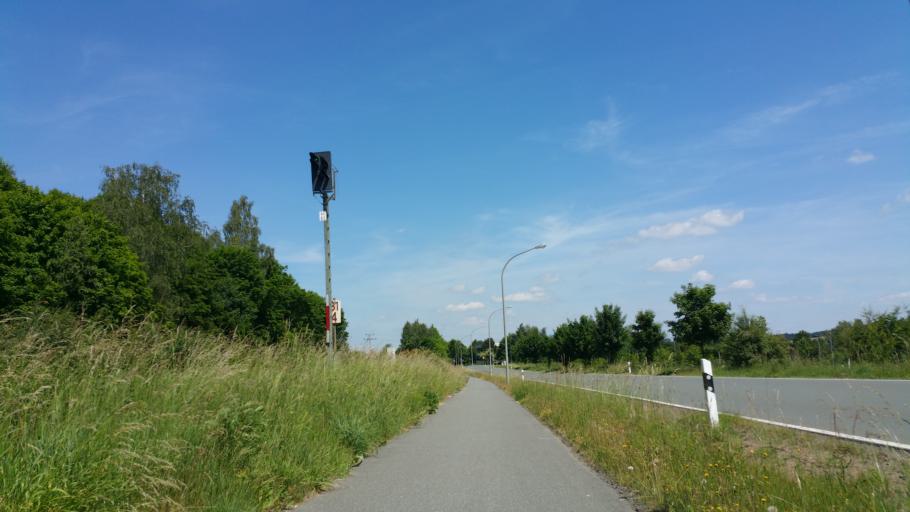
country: DE
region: Bavaria
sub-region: Upper Franconia
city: Schwarzenbach an der Saale
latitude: 50.2211
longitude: 11.9534
